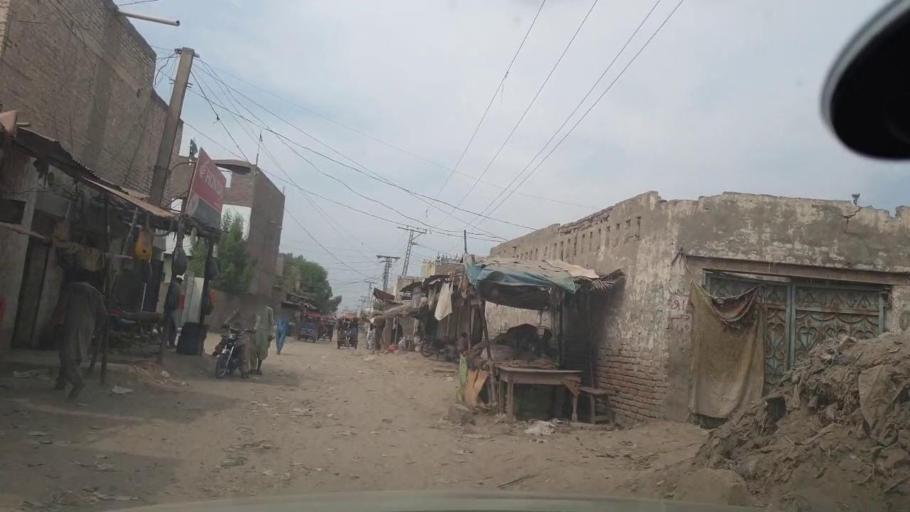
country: PK
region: Sindh
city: Jacobabad
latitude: 28.2701
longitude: 68.4379
